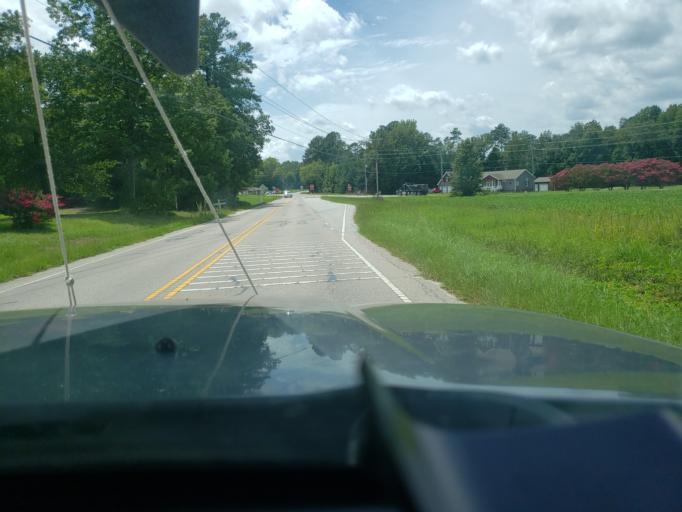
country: US
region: North Carolina
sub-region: Wake County
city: Rolesville
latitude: 35.8799
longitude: -78.4483
